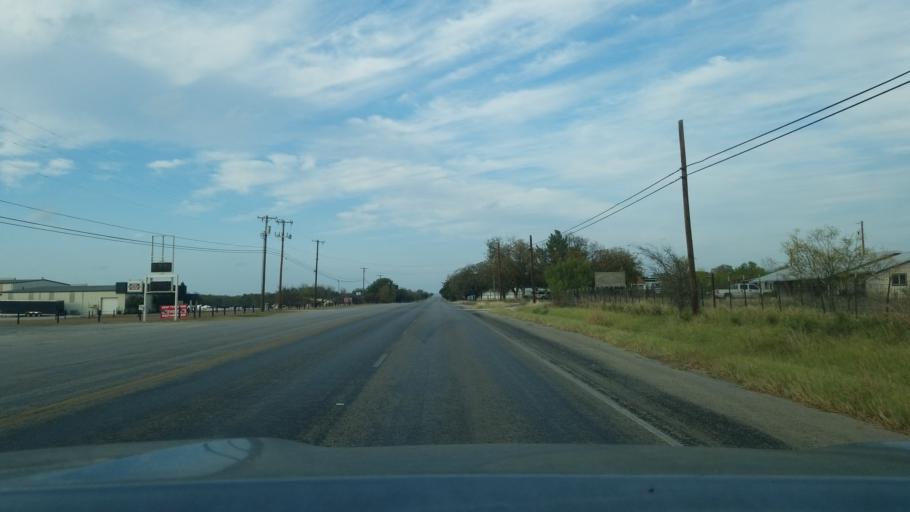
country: US
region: Texas
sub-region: Brown County
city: Early
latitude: 31.7565
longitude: -98.9597
